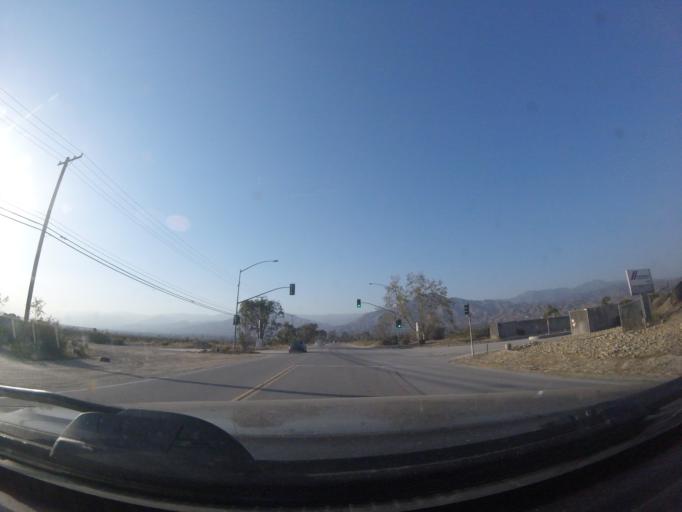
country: US
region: California
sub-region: San Bernardino County
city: Highland
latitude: 34.0984
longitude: -117.1824
